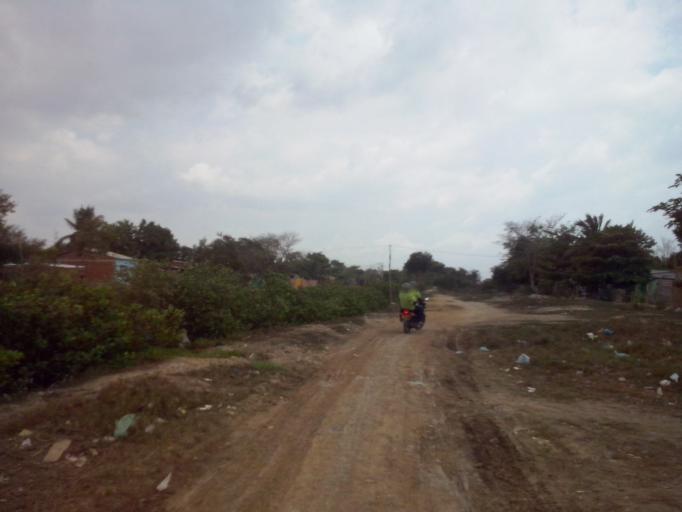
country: CO
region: Bolivar
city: Cartagena
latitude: 10.4155
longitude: -75.4663
